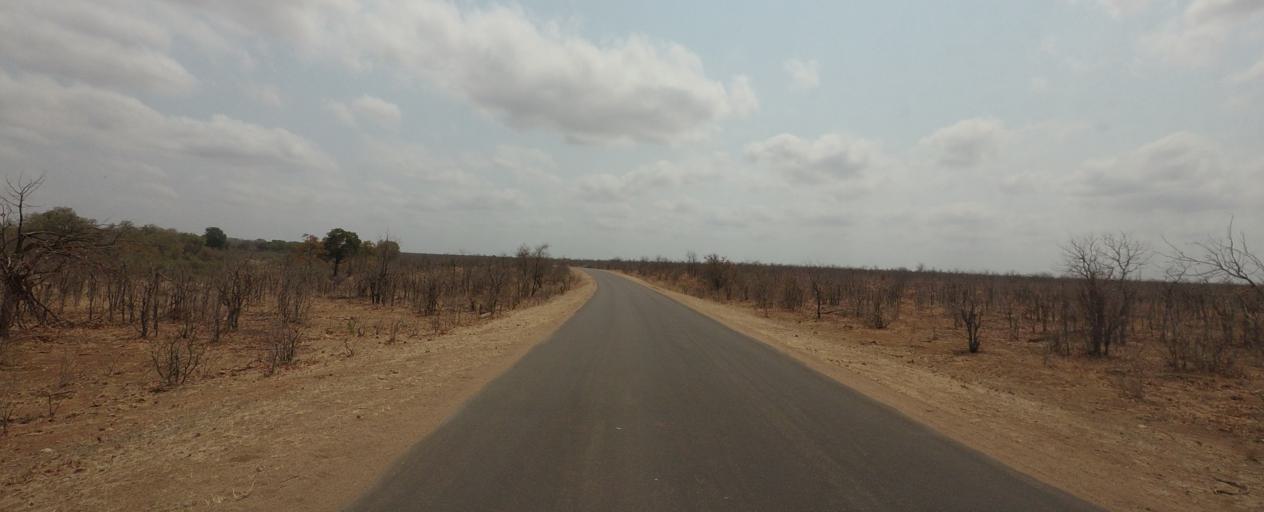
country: ZA
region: Limpopo
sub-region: Mopani District Municipality
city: Phalaborwa
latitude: -23.5455
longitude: 31.4283
